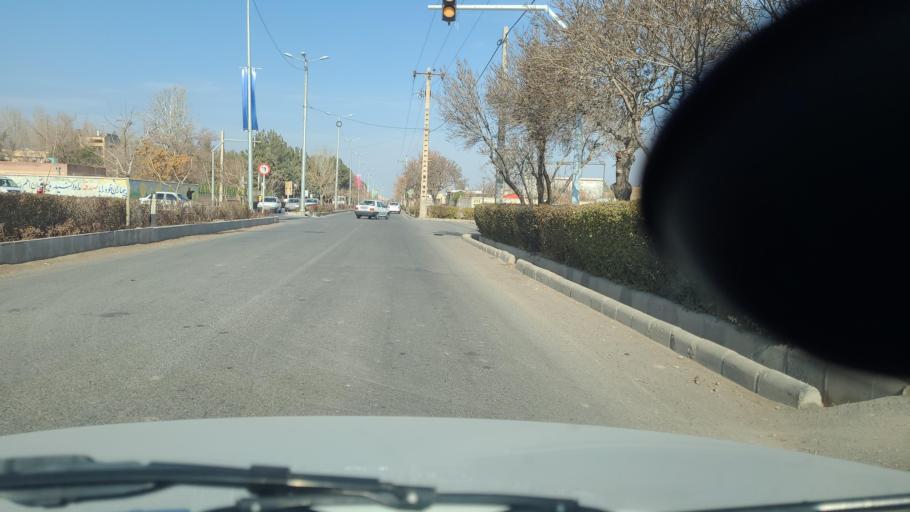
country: IR
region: Razavi Khorasan
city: Fariman
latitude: 35.6888
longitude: 59.8439
